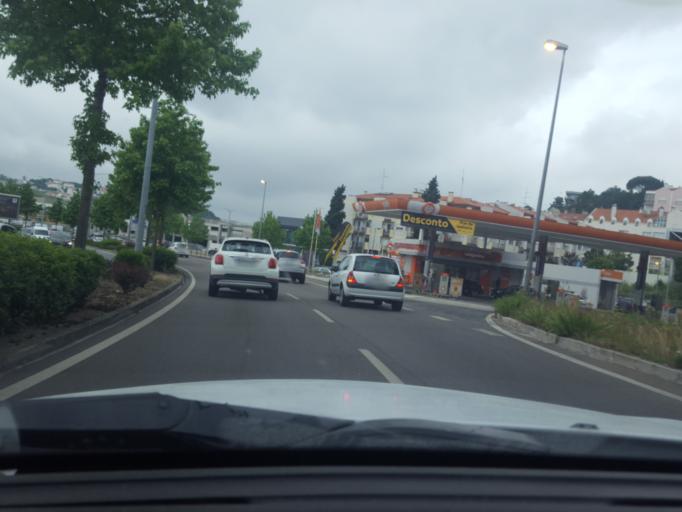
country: PT
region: Leiria
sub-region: Leiria
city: Leiria
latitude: 39.7386
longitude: -8.8148
